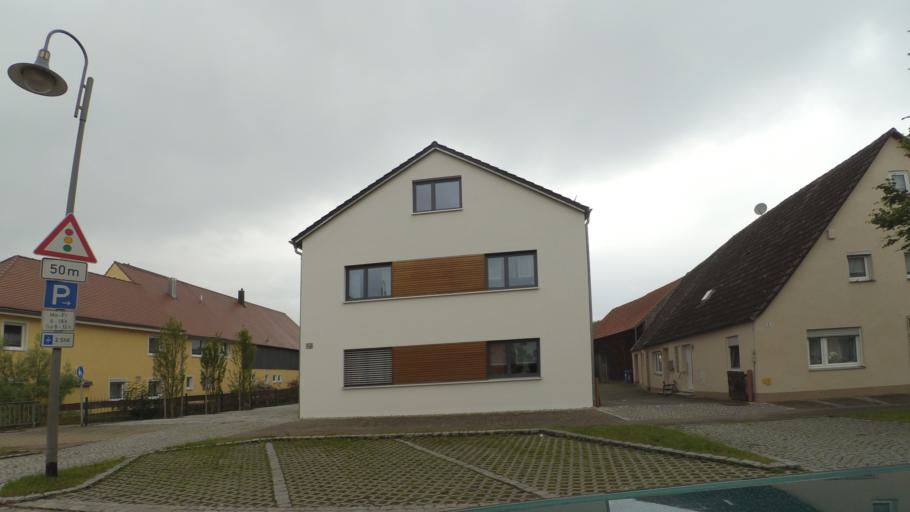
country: DE
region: Bavaria
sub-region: Swabia
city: Monheim
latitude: 48.8437
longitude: 10.8576
